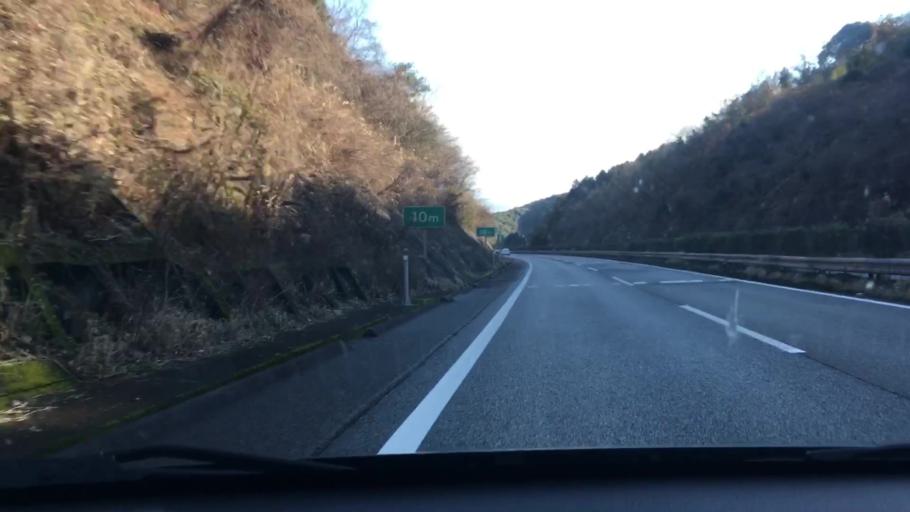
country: JP
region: Kumamoto
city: Hitoyoshi
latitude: 32.1737
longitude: 130.7901
